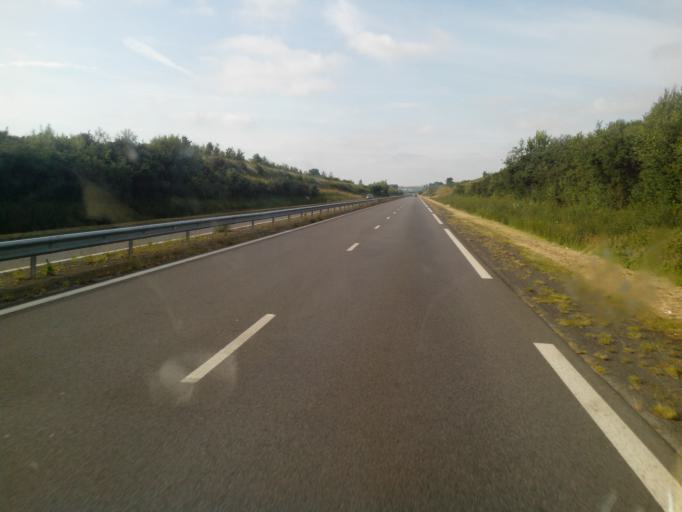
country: FR
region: Brittany
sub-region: Departement d'Ille-et-Vilaine
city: Betton
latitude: 48.1689
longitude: -1.6265
